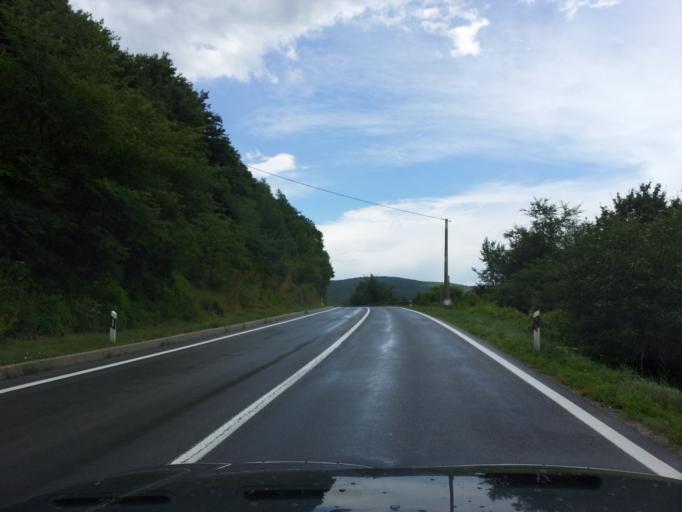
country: BA
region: Federation of Bosnia and Herzegovina
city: Bihac
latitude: 44.6378
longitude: 15.7220
